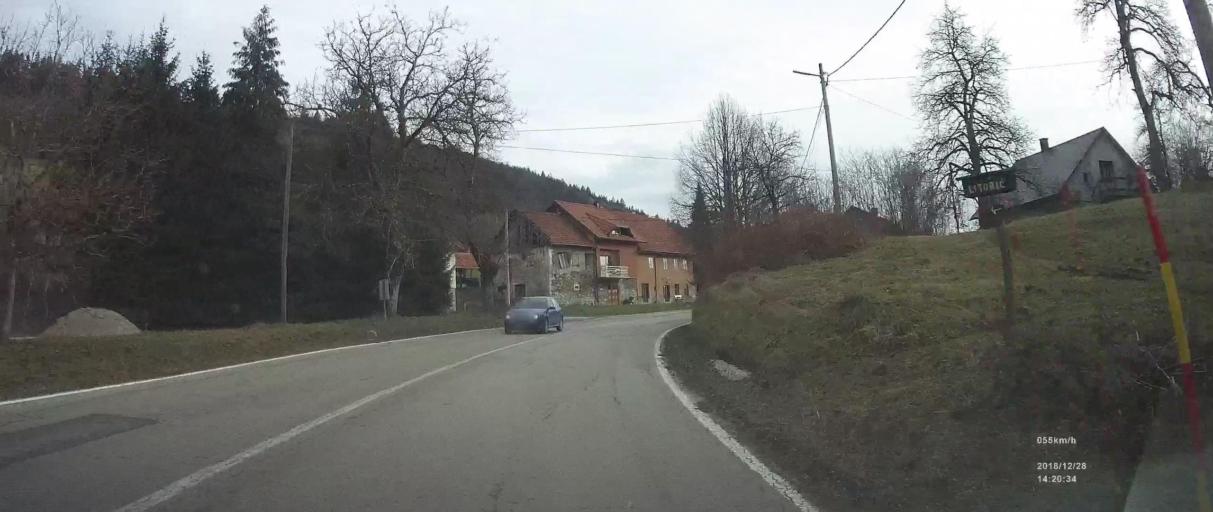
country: HR
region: Primorsko-Goranska
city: Vrbovsko
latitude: 45.4001
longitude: 15.0765
